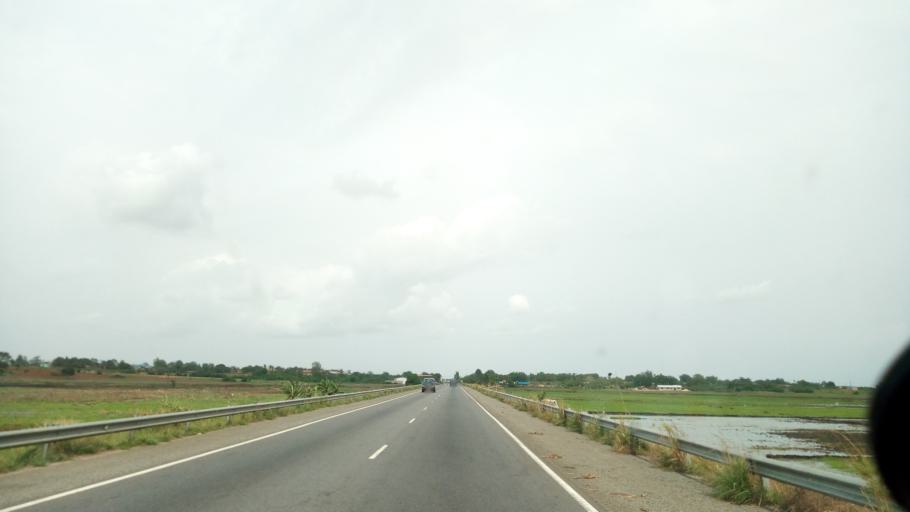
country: GH
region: Volta
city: Keta
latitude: 6.0611
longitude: 0.9369
